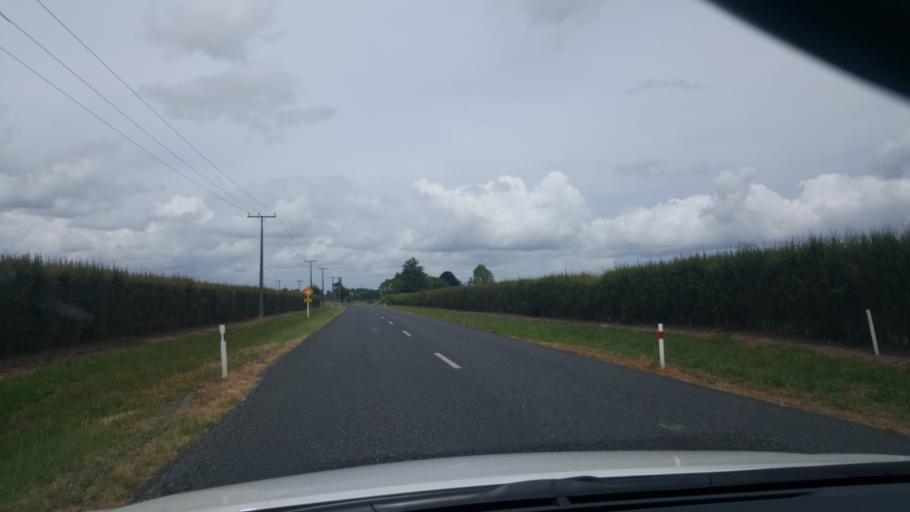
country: NZ
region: Waikato
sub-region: Matamata-Piako District
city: Matamata
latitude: -37.8811
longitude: 175.7305
